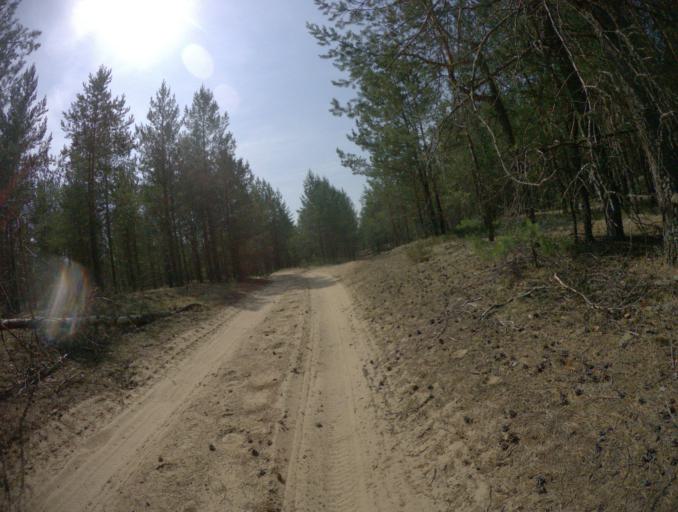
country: RU
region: Ivanovo
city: Talitsy
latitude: 56.4114
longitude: 42.3789
